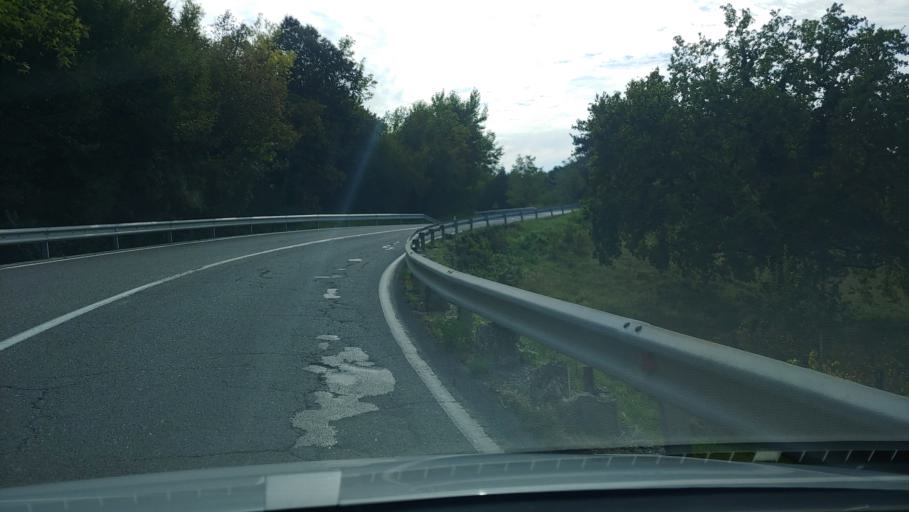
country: SI
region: Nova Gorica
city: Sempas
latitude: 45.9126
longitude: 13.7680
